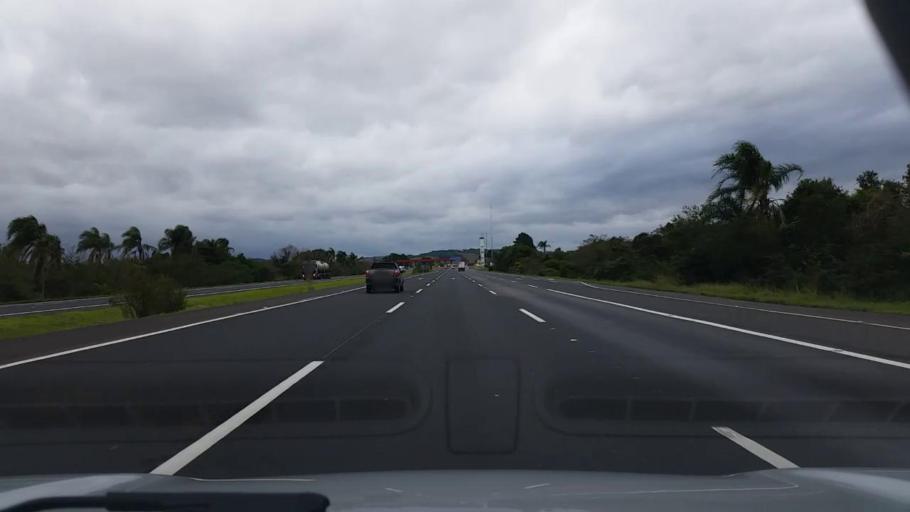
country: BR
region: Rio Grande do Sul
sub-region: Osorio
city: Osorio
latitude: -29.8835
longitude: -50.4420
